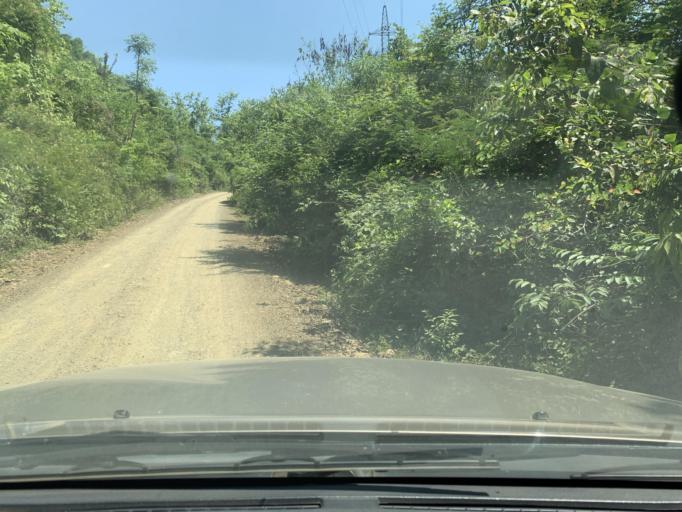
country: LA
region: Louangphabang
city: Louangphabang
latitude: 19.9026
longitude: 102.2182
